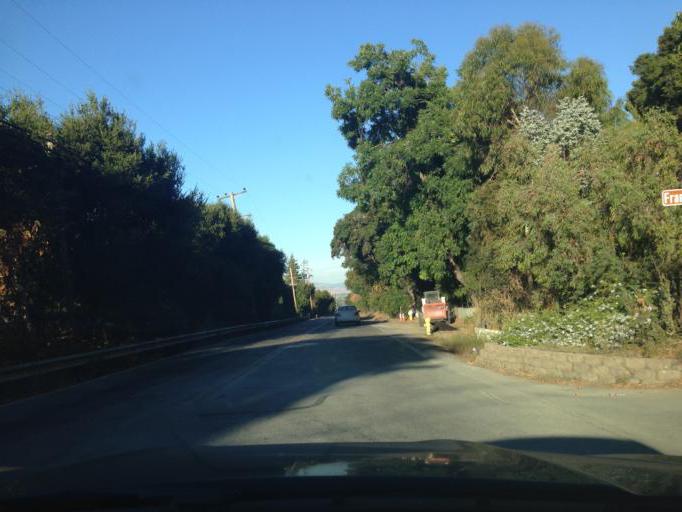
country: US
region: California
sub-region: Santa Clara County
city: Cambrian Park
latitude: 37.2361
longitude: -121.9402
